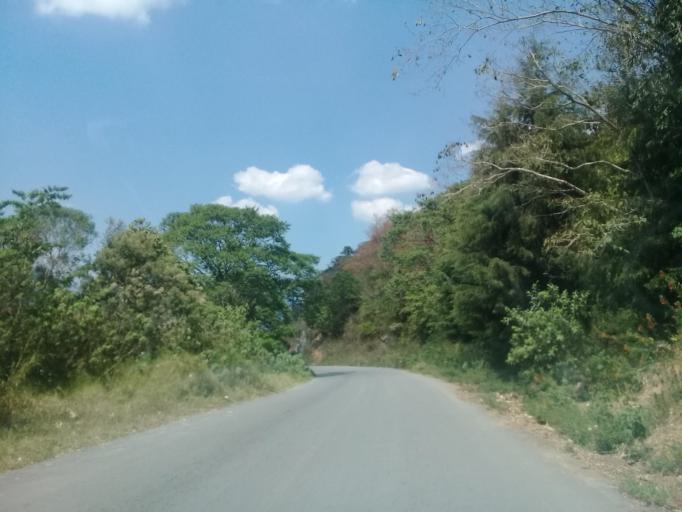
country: MX
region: Veracruz
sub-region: Tlilapan
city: Tonalixco
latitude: 18.8009
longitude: -97.0582
